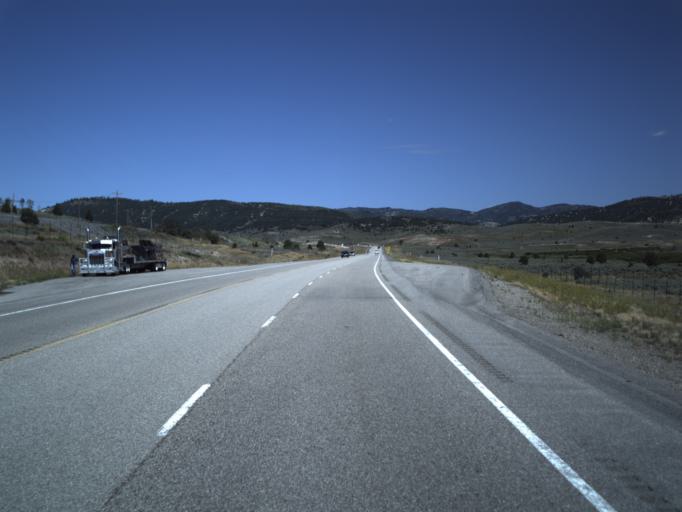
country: US
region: Utah
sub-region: Carbon County
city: Helper
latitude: 39.9061
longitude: -111.0596
